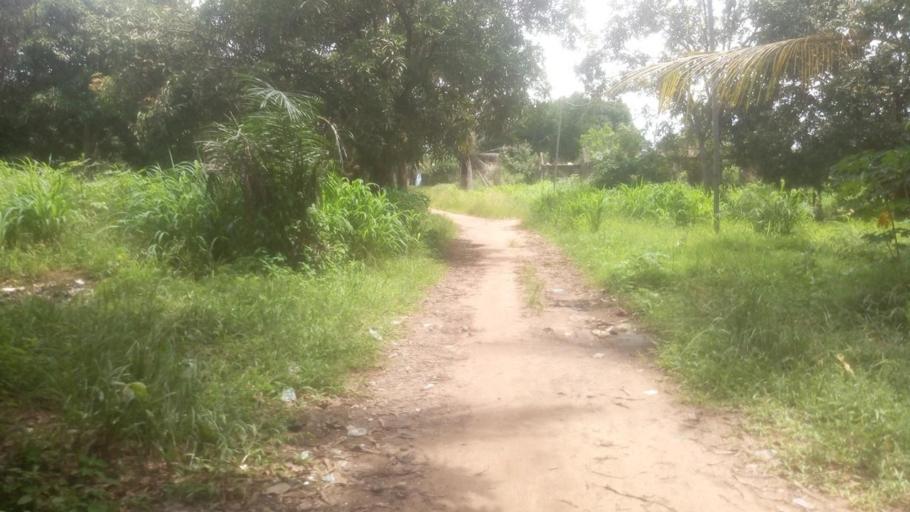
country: SL
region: Northern Province
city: Masoyila
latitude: 8.5473
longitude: -13.1595
